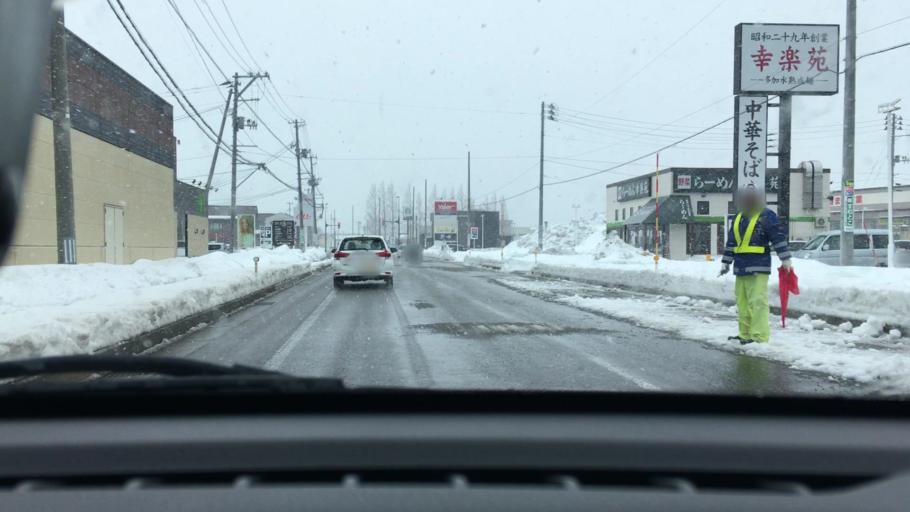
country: JP
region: Niigata
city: Joetsu
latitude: 37.1596
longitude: 138.2534
